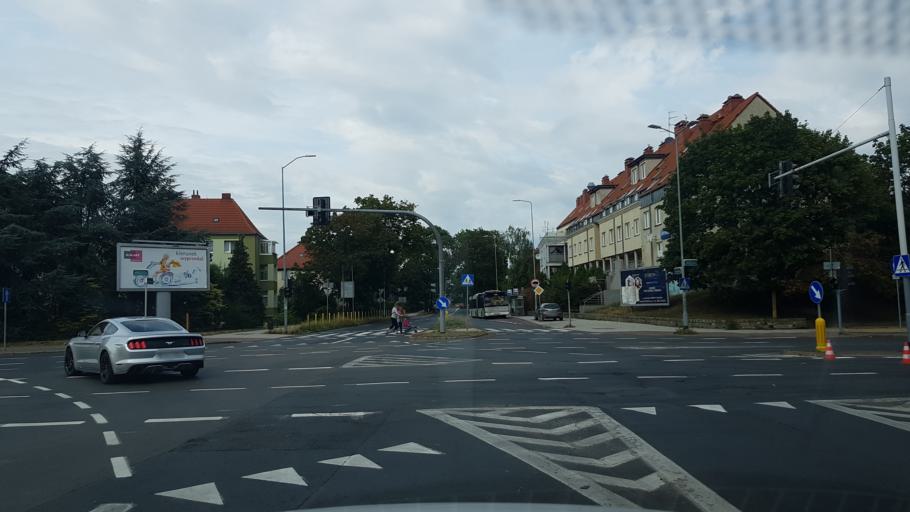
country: PL
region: West Pomeranian Voivodeship
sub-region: Szczecin
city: Szczecin
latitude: 53.4329
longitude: 14.5121
